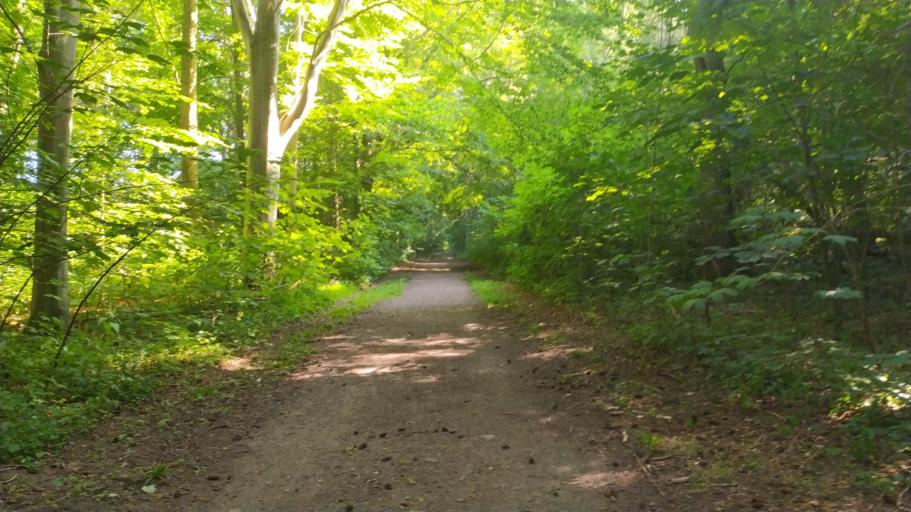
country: DE
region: Schleswig-Holstein
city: Kronshagen
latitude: 54.3651
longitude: 10.1014
